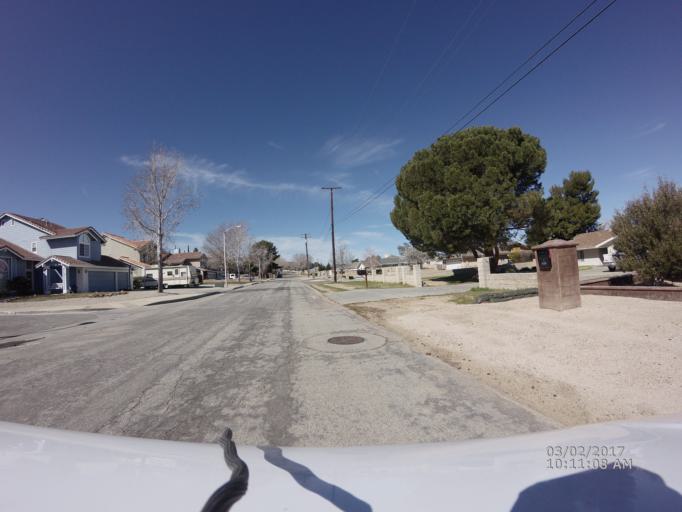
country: US
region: California
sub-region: Los Angeles County
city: Quartz Hill
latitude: 34.6436
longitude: -118.2332
